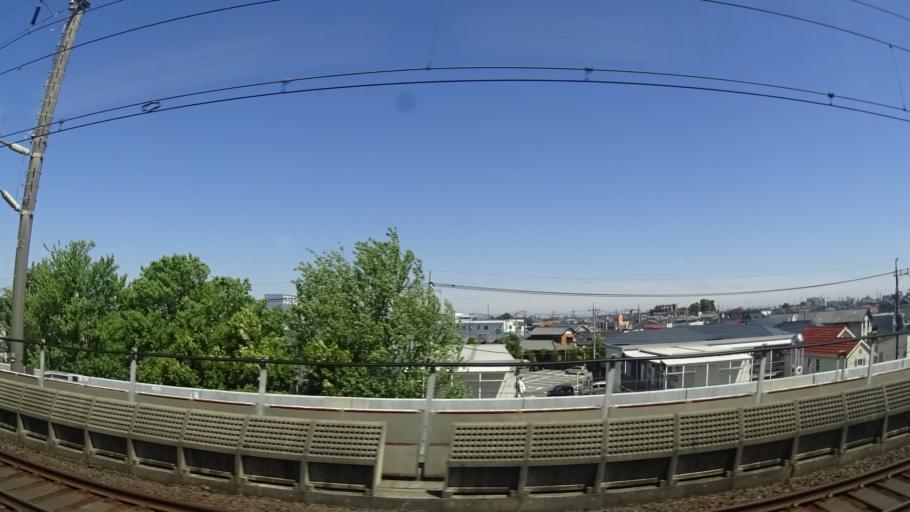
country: JP
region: Saitama
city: Ageoshimo
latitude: 35.9651
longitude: 139.6225
